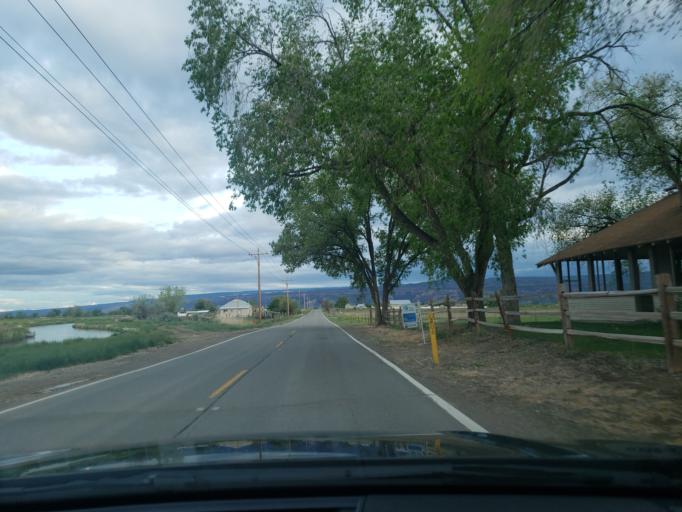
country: US
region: Colorado
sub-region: Mesa County
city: Fruita
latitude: 39.1981
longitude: -108.7012
